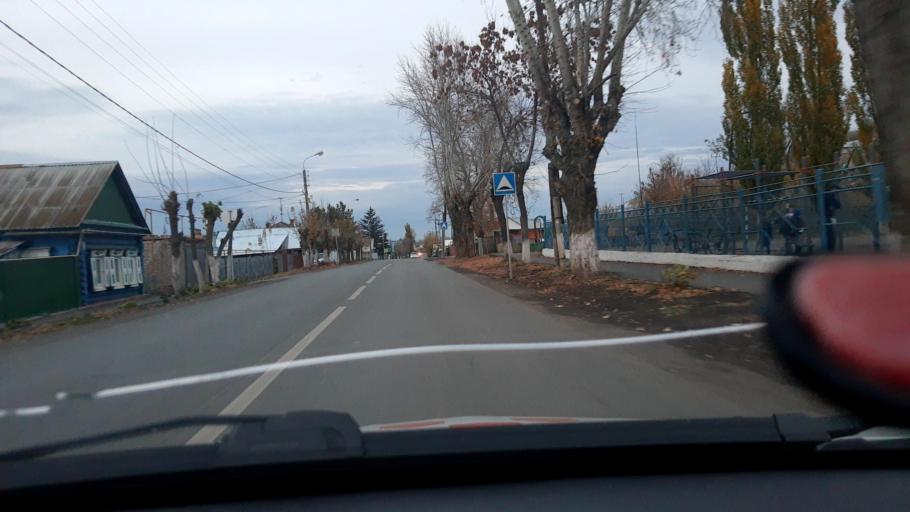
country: RU
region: Bashkortostan
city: Ufa
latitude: 54.7331
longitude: 55.9165
